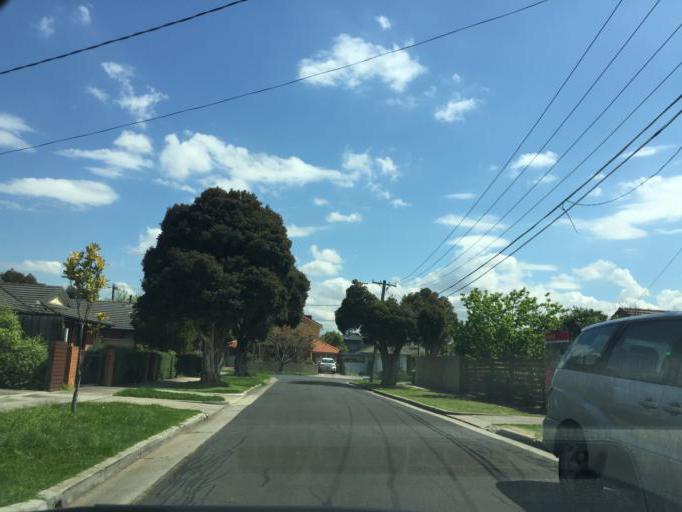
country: AU
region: Victoria
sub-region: Maribyrnong
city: Maidstone
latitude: -37.7859
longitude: 144.8707
